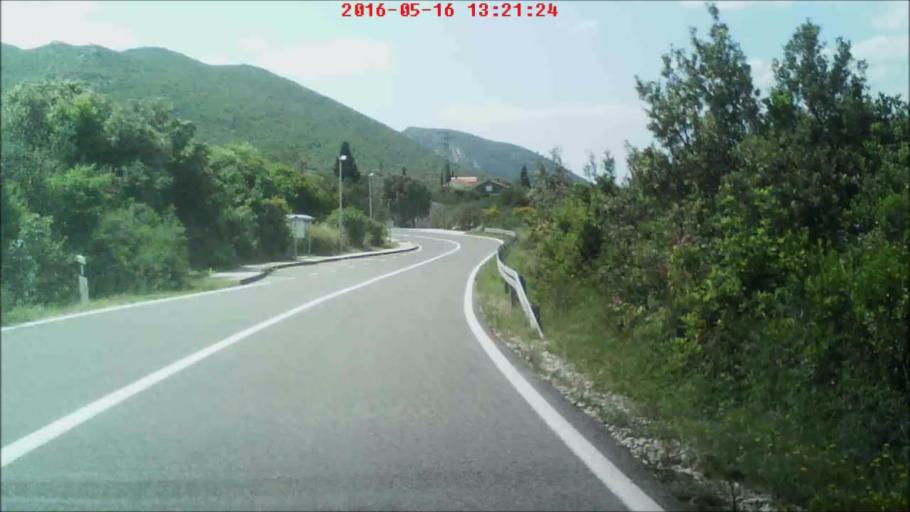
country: HR
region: Dubrovacko-Neretvanska
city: Ston
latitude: 42.8311
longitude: 17.7333
